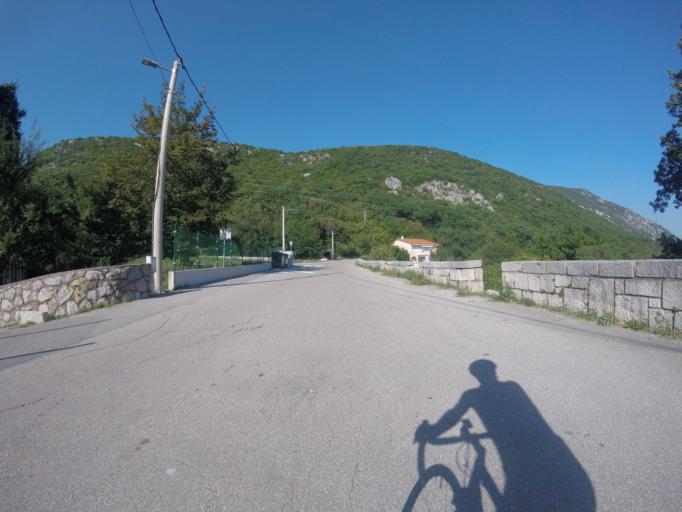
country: HR
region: Primorsko-Goranska
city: Hreljin
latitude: 45.2598
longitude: 14.6147
